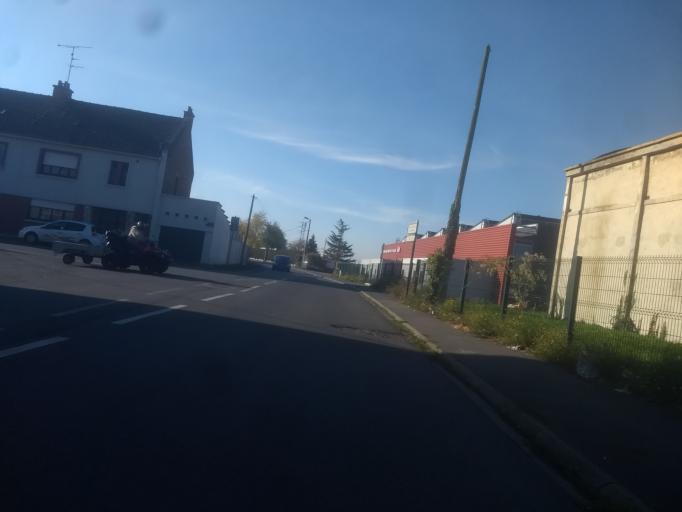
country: FR
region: Nord-Pas-de-Calais
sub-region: Departement du Pas-de-Calais
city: Arras
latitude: 50.2809
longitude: 2.7734
